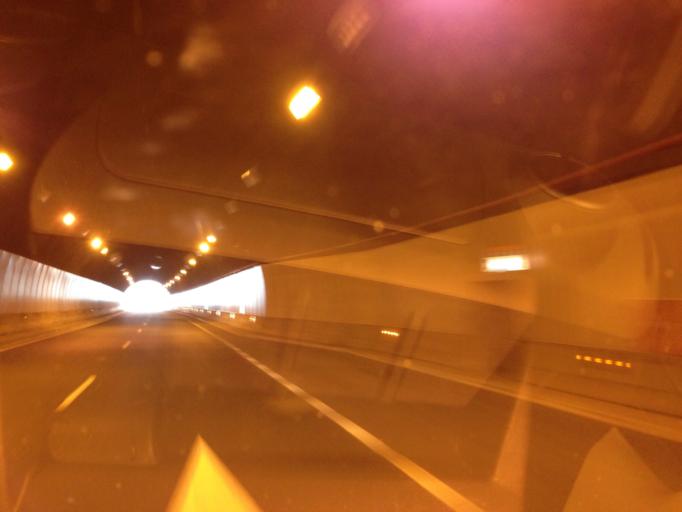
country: ES
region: Canary Islands
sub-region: Provincia de Las Palmas
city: Puerto Rico
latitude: 27.7870
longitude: -15.6907
